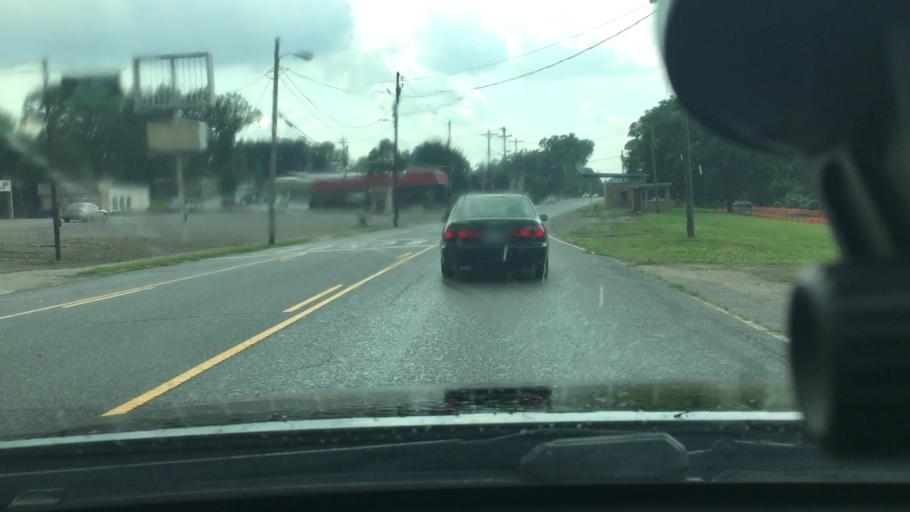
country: US
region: North Carolina
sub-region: Rutherford County
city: Spindale
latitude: 35.3586
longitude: -81.9339
